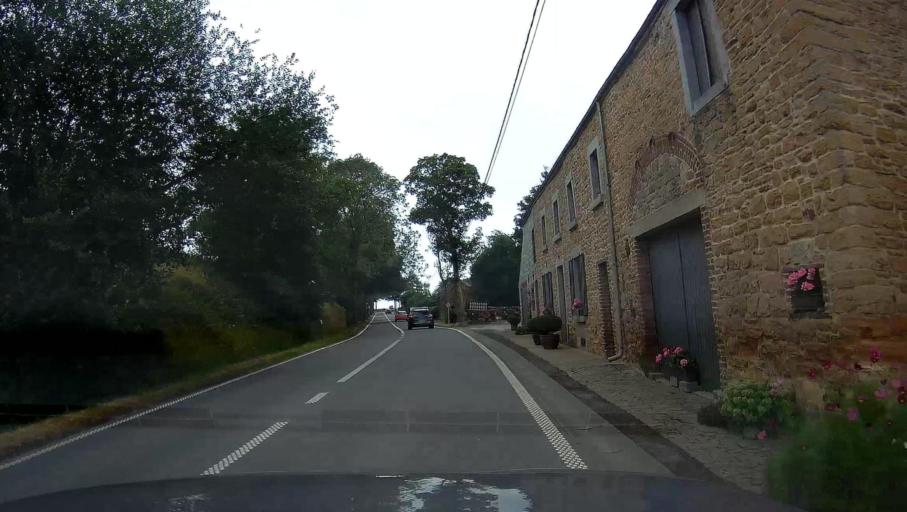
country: BE
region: Wallonia
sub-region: Province de Namur
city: Assesse
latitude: 50.3506
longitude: 5.0446
